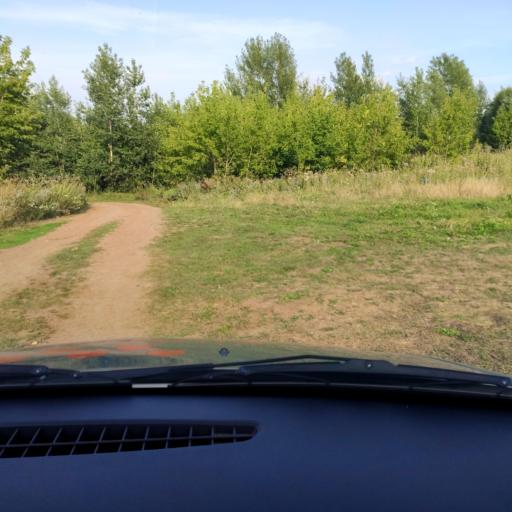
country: RU
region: Bashkortostan
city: Ufa
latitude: 54.6094
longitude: 55.9677
